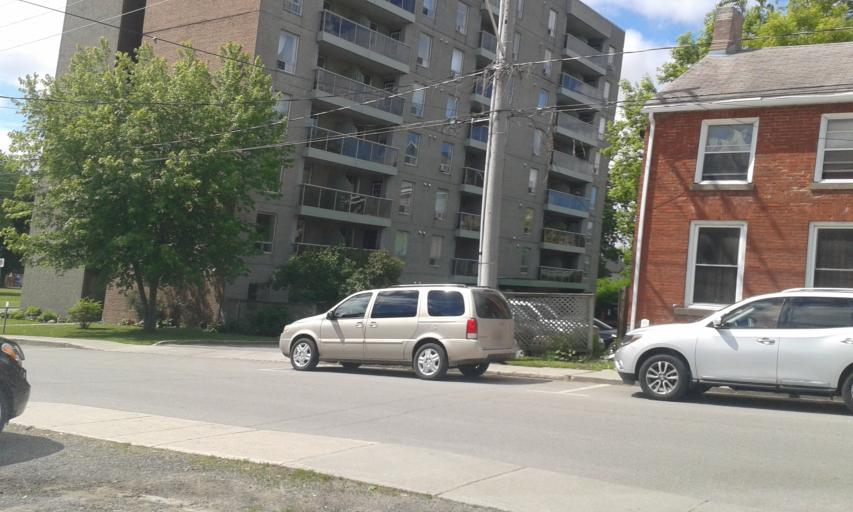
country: CA
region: Ontario
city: Brockville
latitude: 44.5879
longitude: -75.6856
